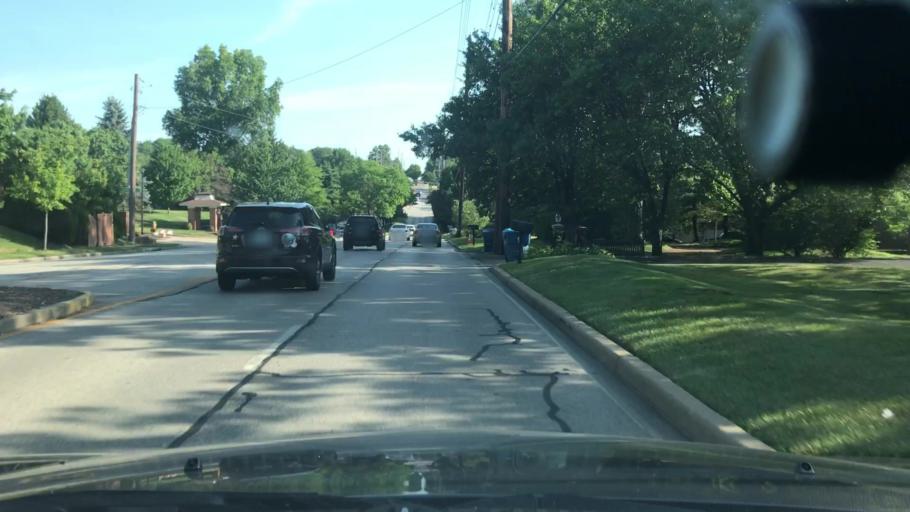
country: US
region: Missouri
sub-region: Saint Louis County
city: Creve Coeur
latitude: 38.6524
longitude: -90.4433
